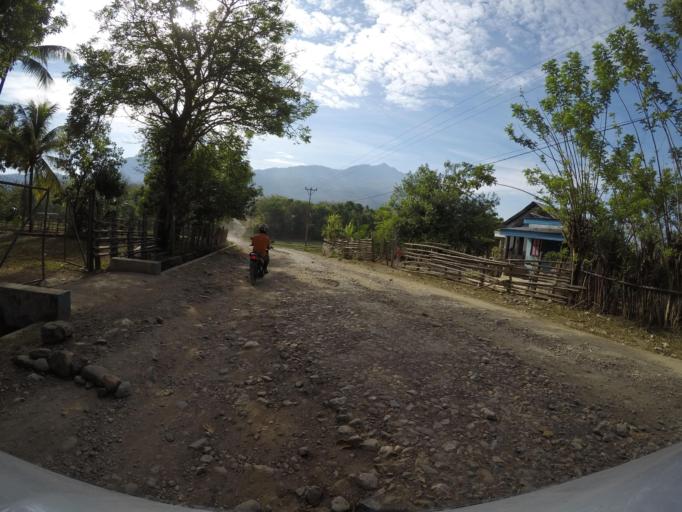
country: TL
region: Bobonaro
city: Maliana
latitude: -8.9235
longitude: 125.2113
